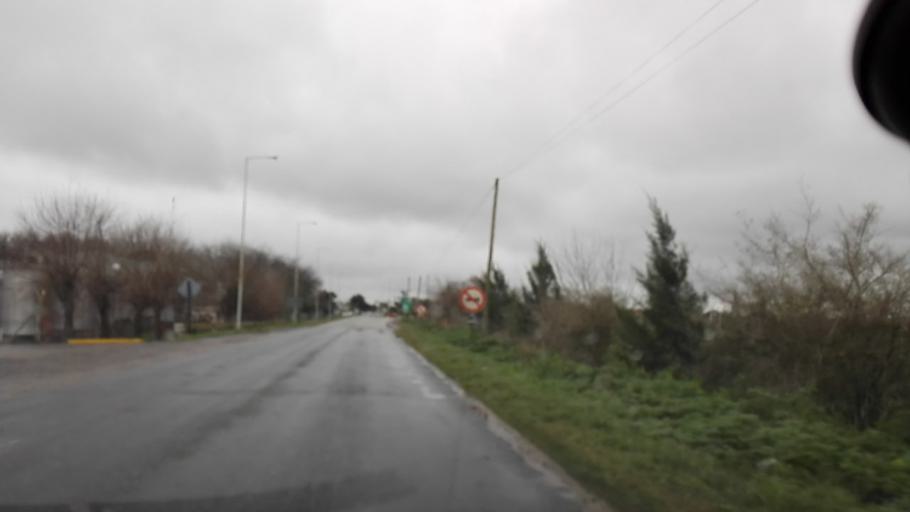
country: AR
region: Buenos Aires
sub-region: Partido de Brandsen
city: Brandsen
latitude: -35.1750
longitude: -58.2448
